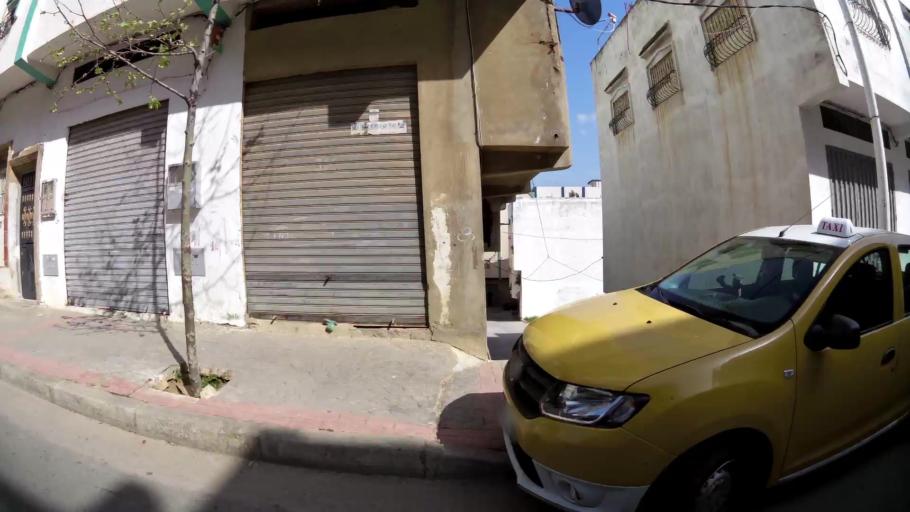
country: MA
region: Tanger-Tetouan
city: Tetouan
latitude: 35.5884
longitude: -5.3586
